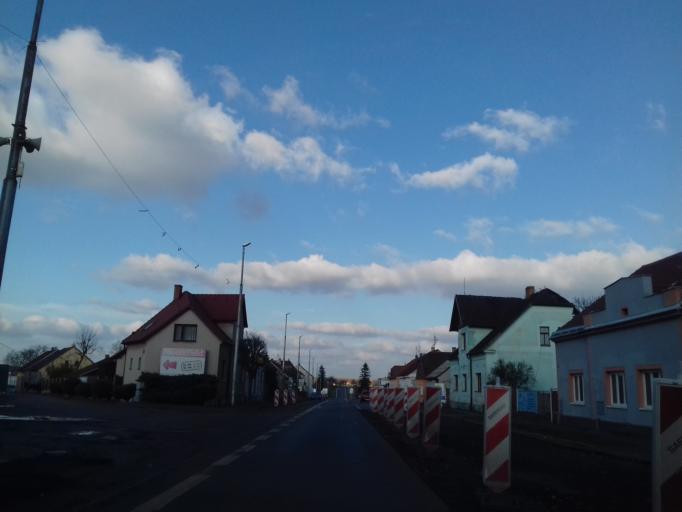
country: CZ
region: Plzensky
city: Chotesov
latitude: 49.6569
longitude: 13.2001
